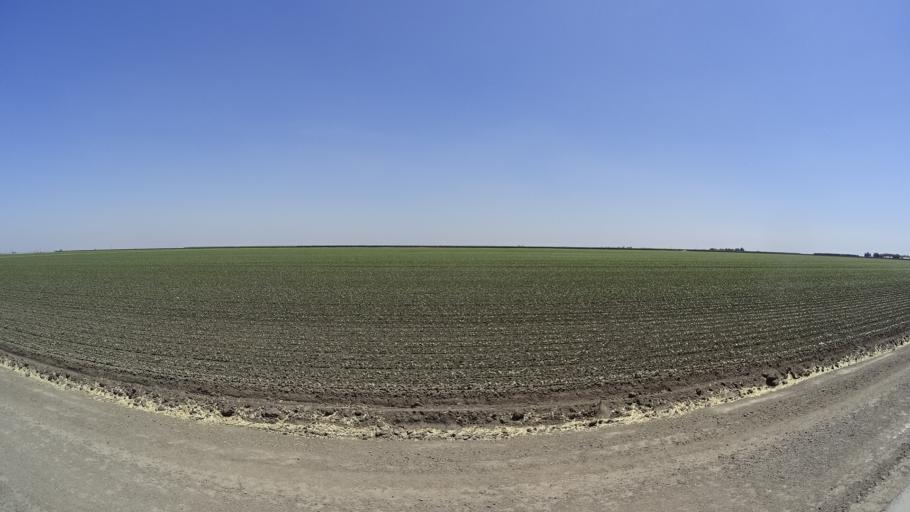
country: US
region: California
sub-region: Kings County
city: Corcoran
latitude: 36.1283
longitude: -119.6444
